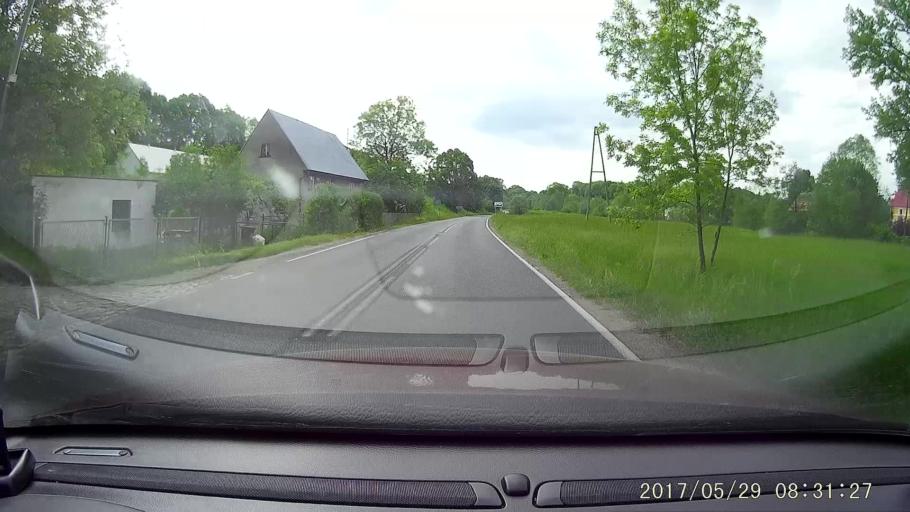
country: PL
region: Lower Silesian Voivodeship
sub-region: Powiat zlotoryjski
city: Swierzawa
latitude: 51.0221
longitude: 15.8825
